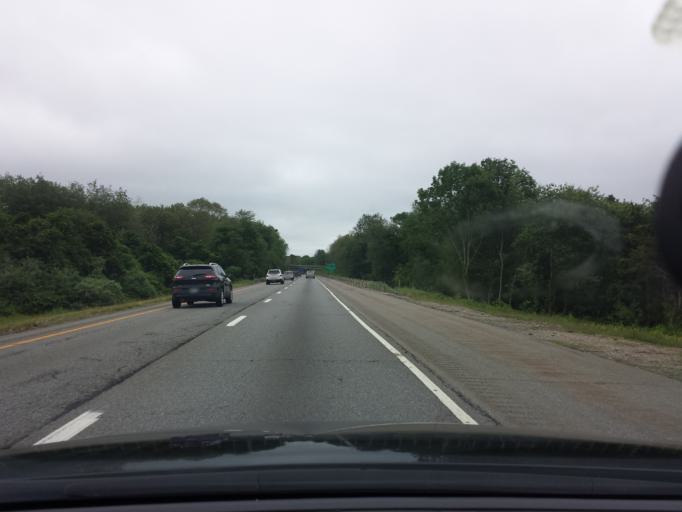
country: US
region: Connecticut
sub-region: New London County
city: Pawcatuck
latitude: 41.3922
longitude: -71.8725
